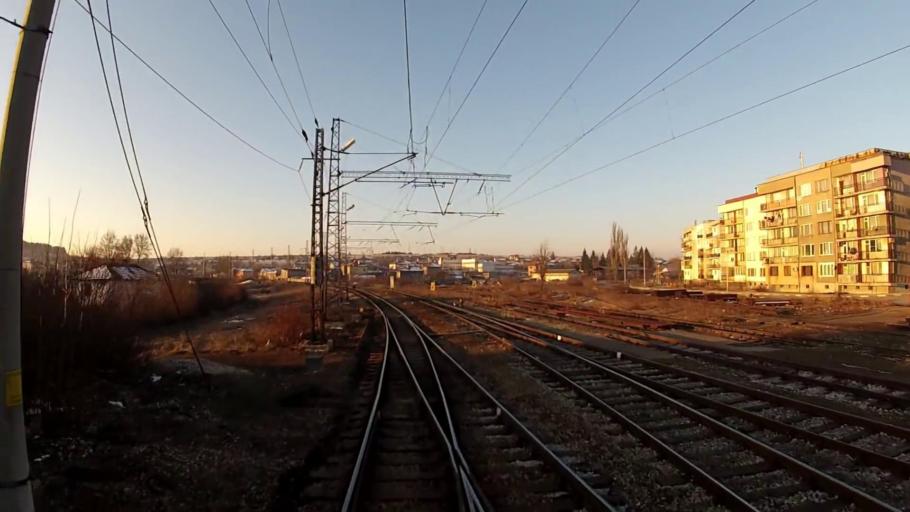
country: BG
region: Sofiya
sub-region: Obshtina Dragoman
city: Dragoman
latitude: 42.9169
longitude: 22.9322
